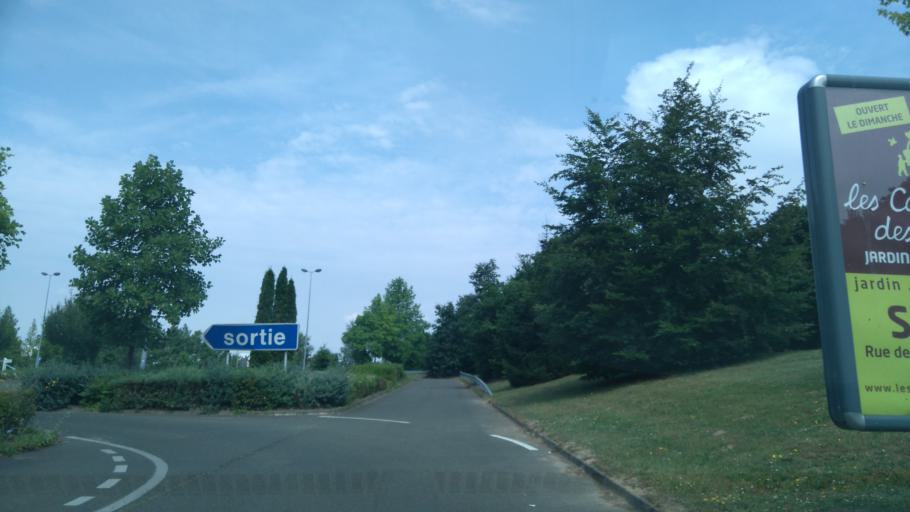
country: FR
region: Picardie
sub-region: Departement de l'Oise
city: Creil
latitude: 49.2376
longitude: 2.4723
